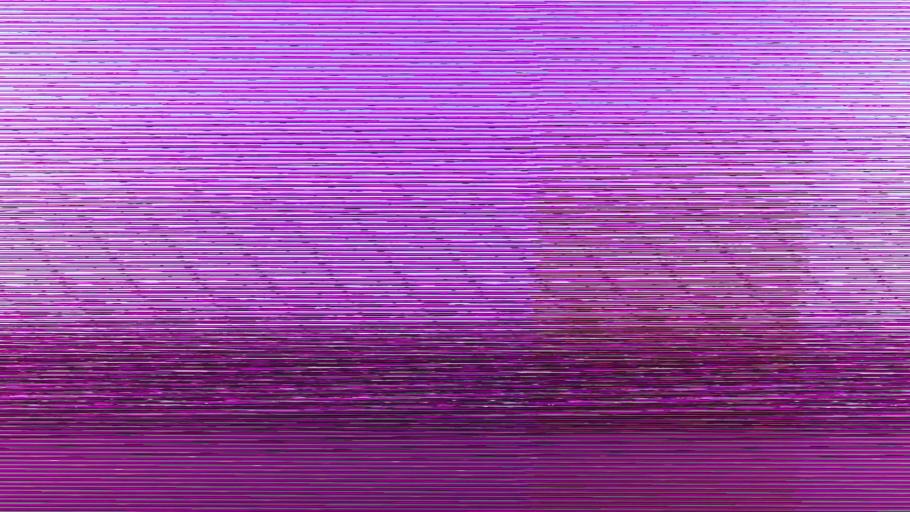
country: US
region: Michigan
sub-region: Oakland County
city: Wolverine Lake
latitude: 42.6491
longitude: -83.5141
